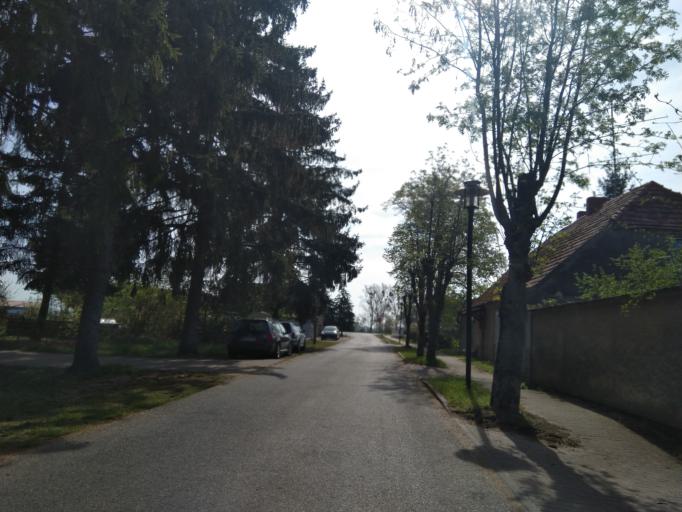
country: DE
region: Brandenburg
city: Wriezen
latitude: 52.7403
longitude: 14.1673
